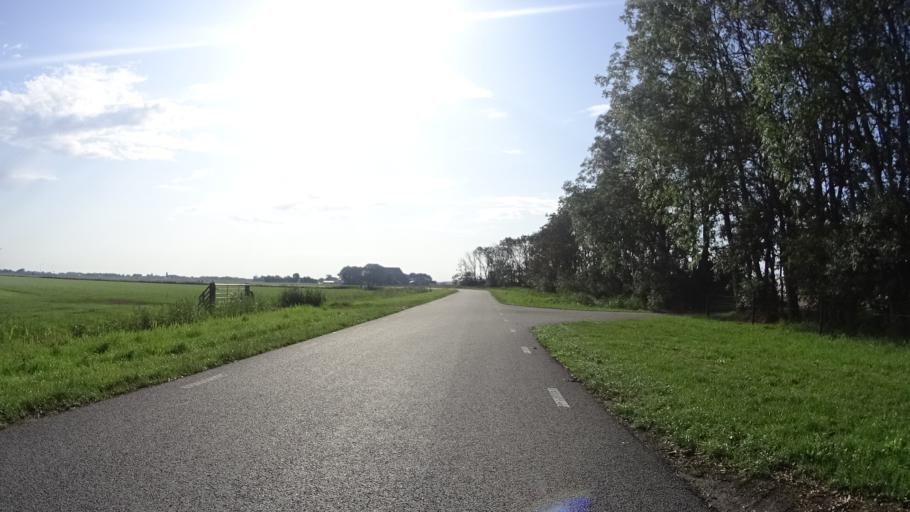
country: NL
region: Friesland
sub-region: Sudwest Fryslan
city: Makkum
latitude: 53.1132
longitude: 5.4068
